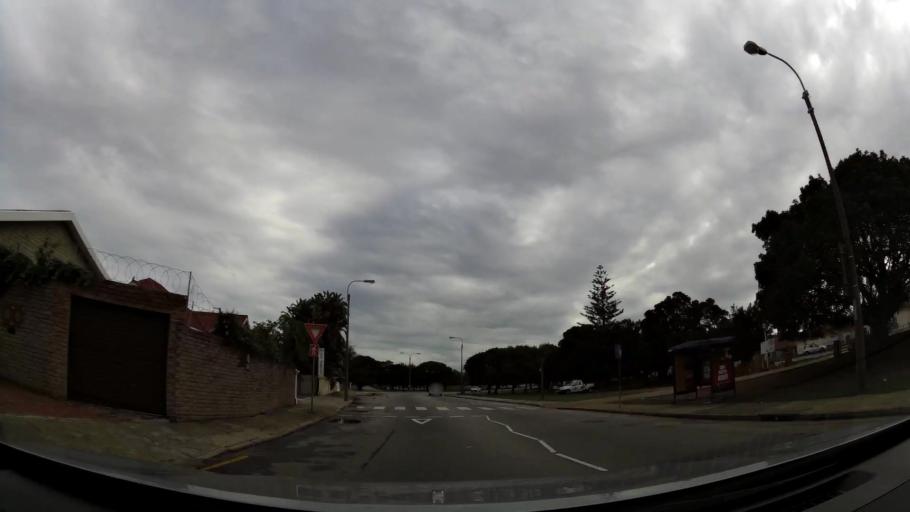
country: ZA
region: Eastern Cape
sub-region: Nelson Mandela Bay Metropolitan Municipality
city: Port Elizabeth
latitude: -33.9588
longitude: 25.5988
